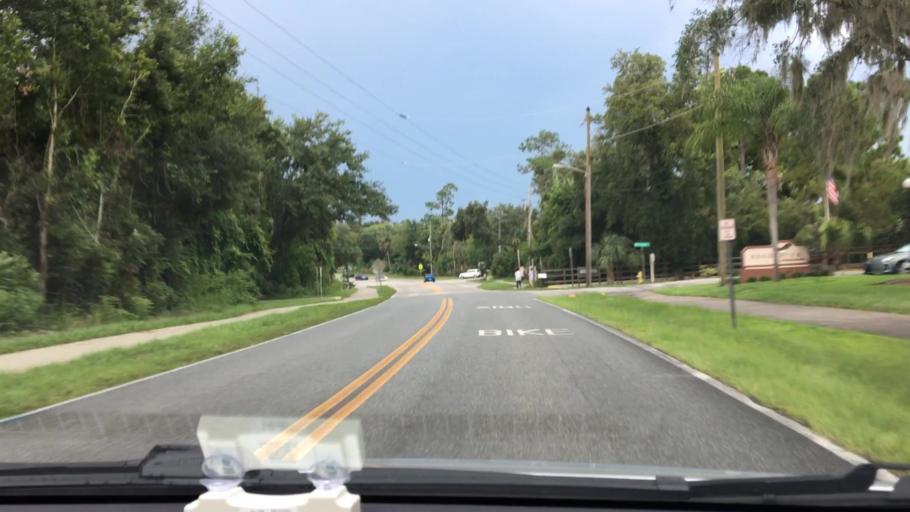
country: US
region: Florida
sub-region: Volusia County
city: Deltona
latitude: 28.8671
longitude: -81.2539
